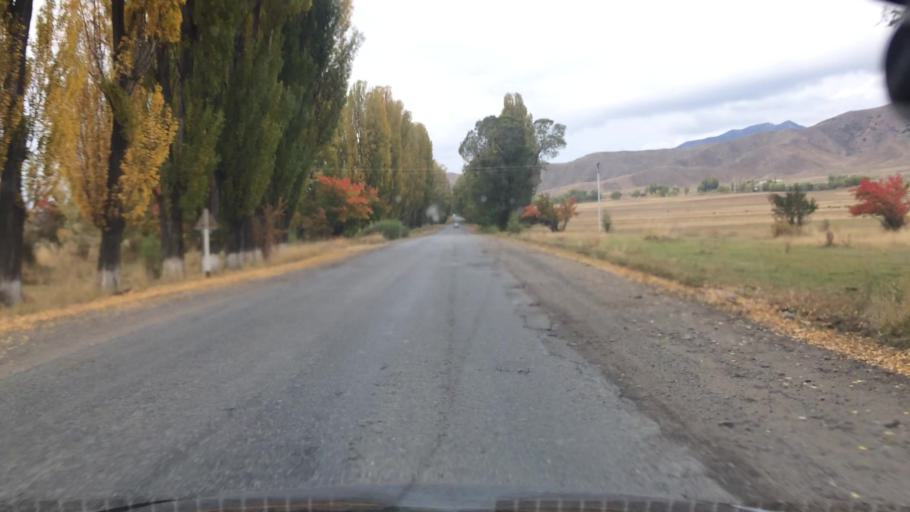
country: KG
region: Ysyk-Koel
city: Pokrovka
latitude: 42.7385
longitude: 77.9169
